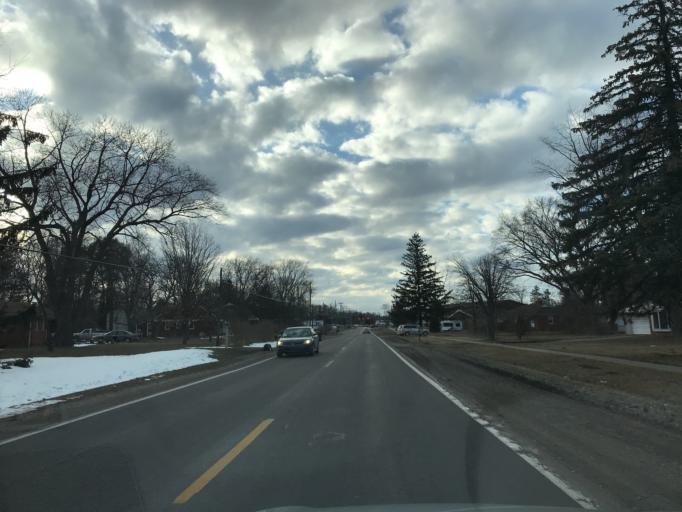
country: US
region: Michigan
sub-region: Oakland County
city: Farmington
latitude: 42.4539
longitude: -83.3326
